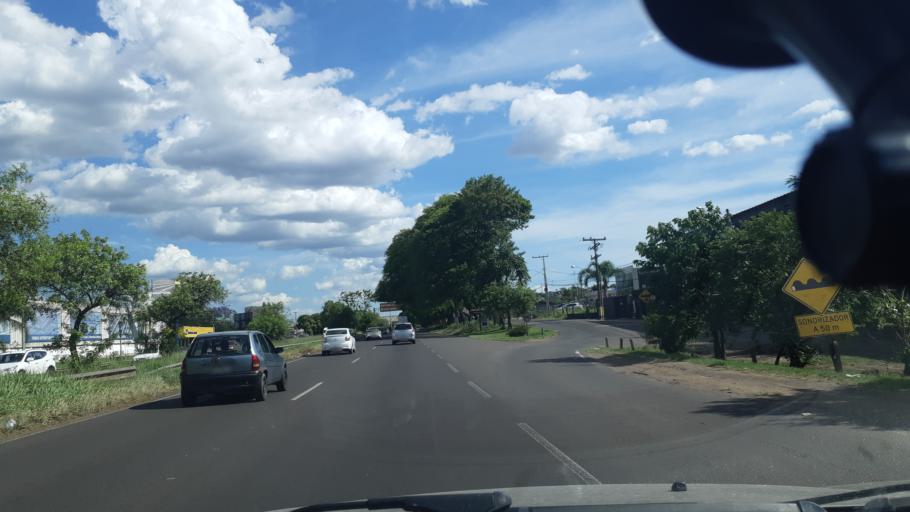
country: BR
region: Rio Grande do Sul
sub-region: Novo Hamburgo
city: Novo Hamburgo
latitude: -29.6588
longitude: -51.1442
